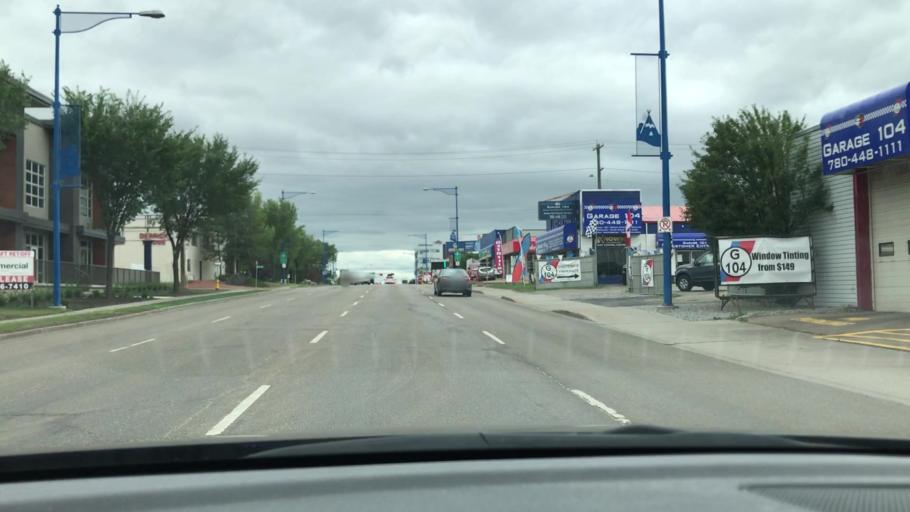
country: CA
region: Alberta
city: Edmonton
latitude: 53.5022
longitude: -113.4977
